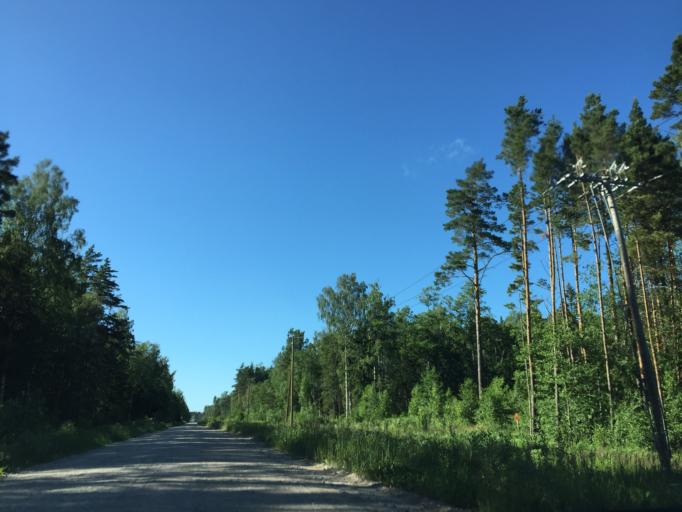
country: LV
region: Ventspils
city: Ventspils
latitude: 57.5519
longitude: 21.7414
